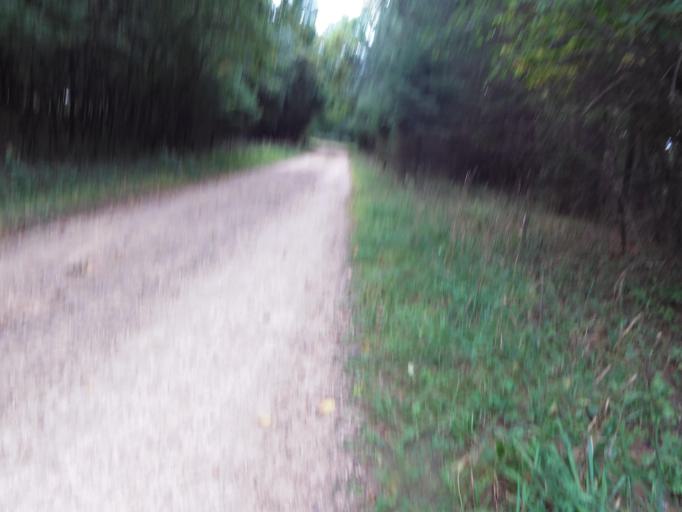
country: US
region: Minnesota
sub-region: Washington County
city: Afton
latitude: 44.8697
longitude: -92.7815
